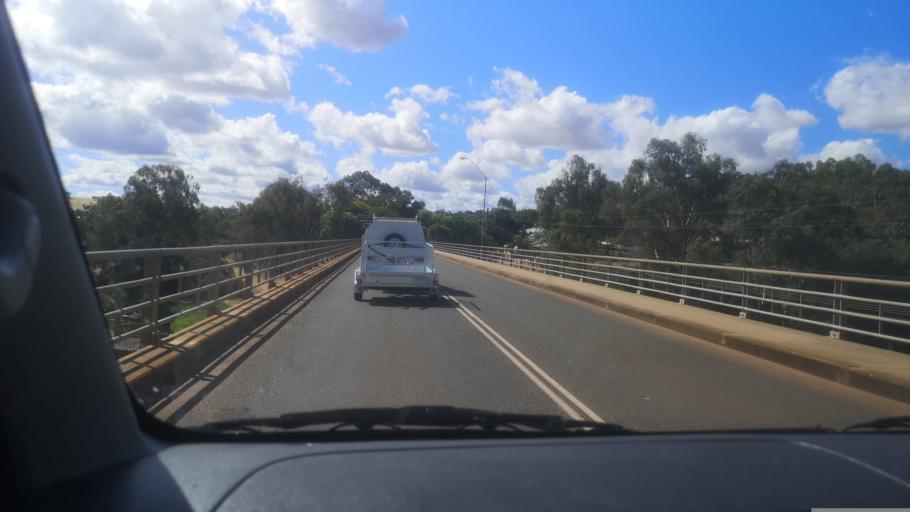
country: AU
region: Western Australia
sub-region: Toodyay
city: Toodyay
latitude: -31.5496
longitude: 116.4633
